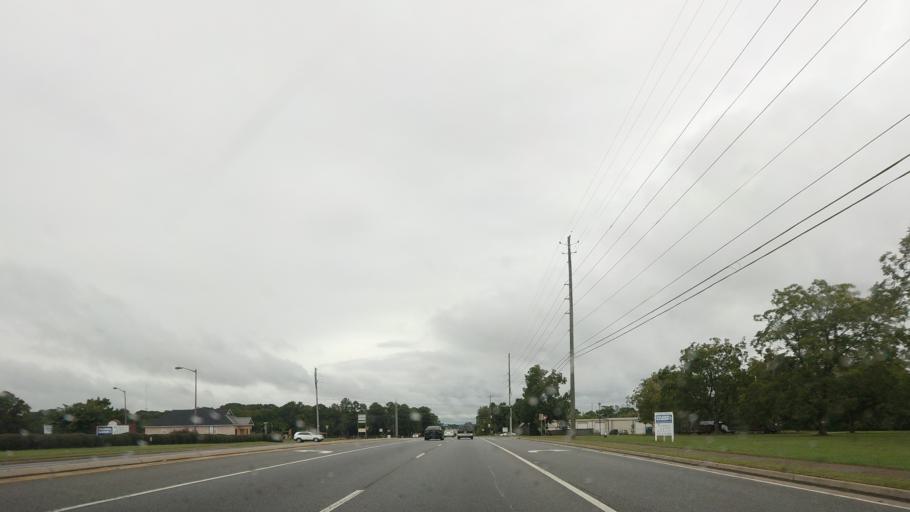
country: US
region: Georgia
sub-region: Houston County
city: Centerville
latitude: 32.5608
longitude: -83.6620
